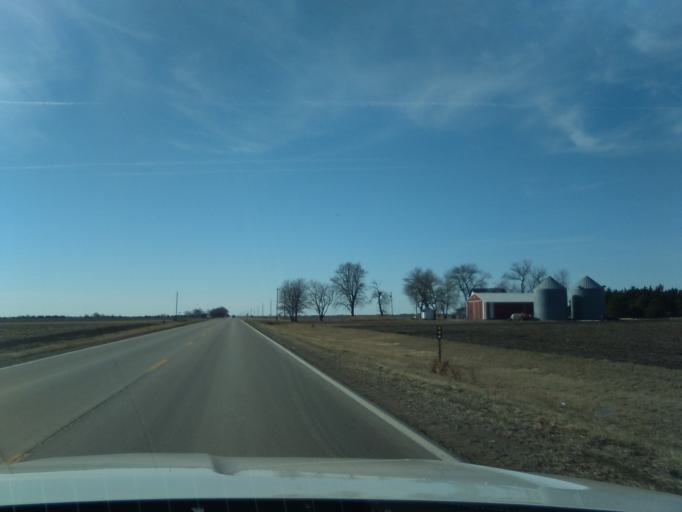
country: US
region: Nebraska
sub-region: Saline County
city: Friend
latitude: 40.8165
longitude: -97.2920
